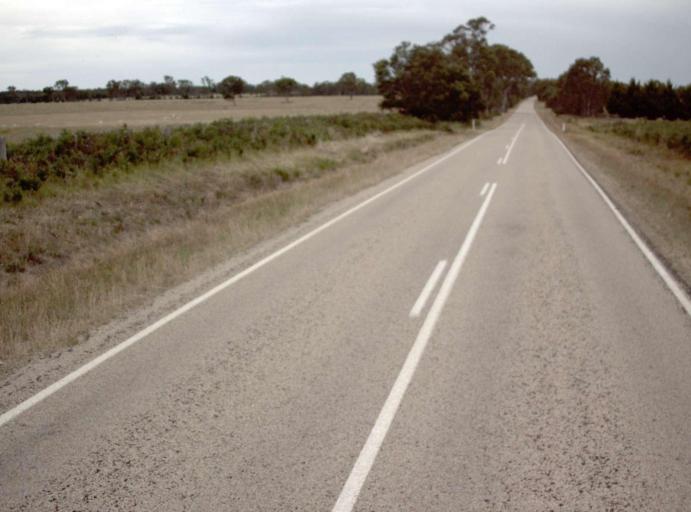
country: AU
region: Victoria
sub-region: East Gippsland
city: Bairnsdale
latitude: -37.9115
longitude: 147.5507
